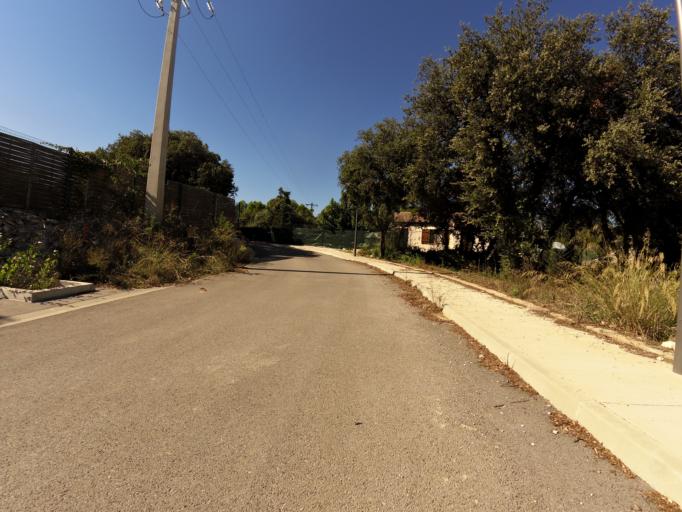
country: FR
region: Languedoc-Roussillon
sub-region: Departement du Gard
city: Aubais
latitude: 43.7571
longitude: 4.1550
